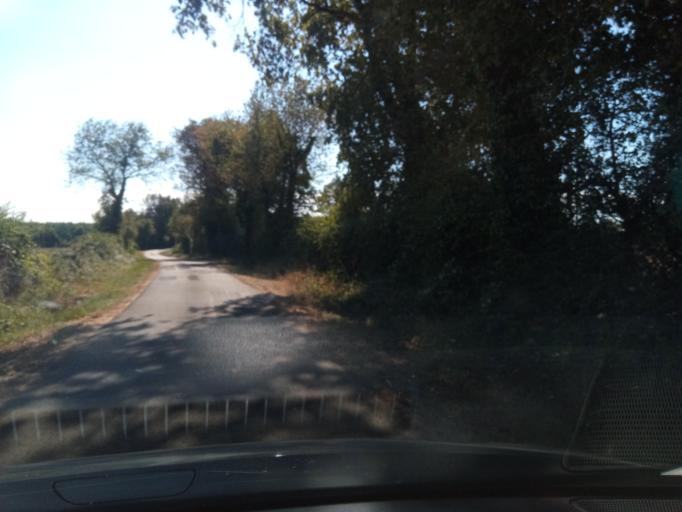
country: FR
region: Poitou-Charentes
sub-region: Departement de la Vienne
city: Lussac-les-Chateaux
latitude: 46.3893
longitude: 0.7646
